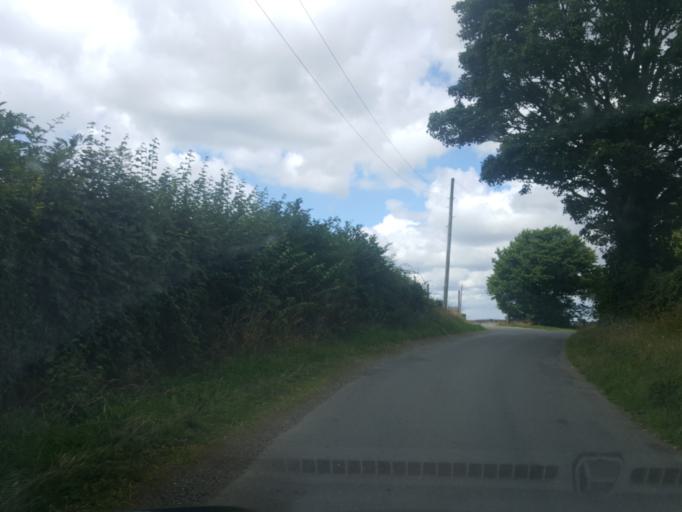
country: IE
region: Leinster
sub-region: County Carlow
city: Carlow
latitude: 52.8973
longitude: -6.9231
